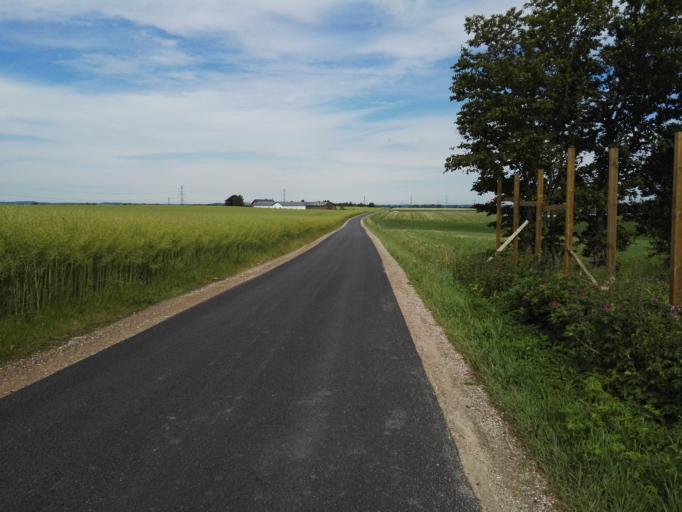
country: DK
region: Capital Region
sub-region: Egedal Kommune
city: Olstykke
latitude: 55.8166
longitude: 12.1727
